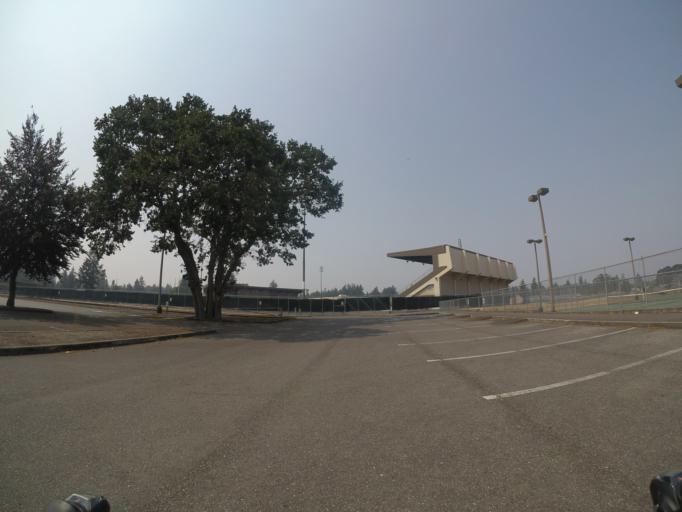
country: US
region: Washington
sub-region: Pierce County
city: Lakewood
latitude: 47.1580
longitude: -122.5155
